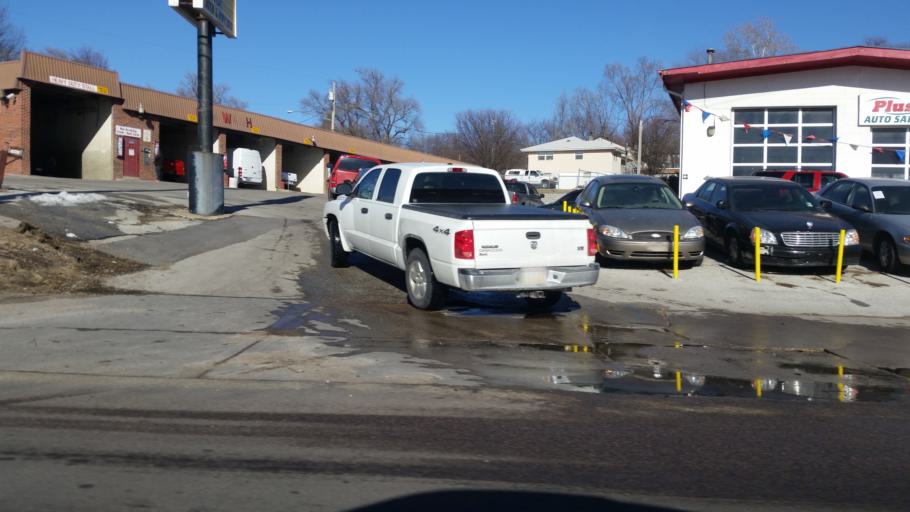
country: US
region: Nebraska
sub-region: Sarpy County
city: Bellevue
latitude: 41.1847
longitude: -95.9320
